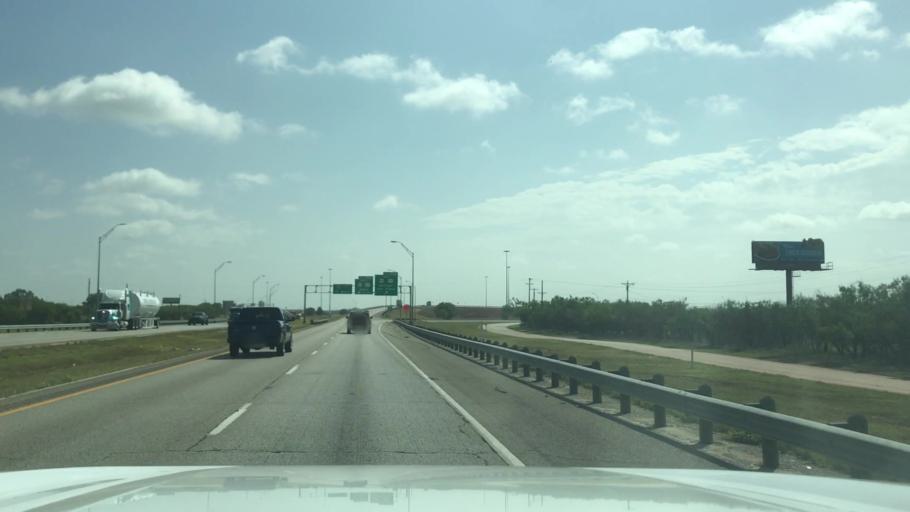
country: US
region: Texas
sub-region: Taylor County
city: Abilene
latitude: 32.4801
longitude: -99.7790
